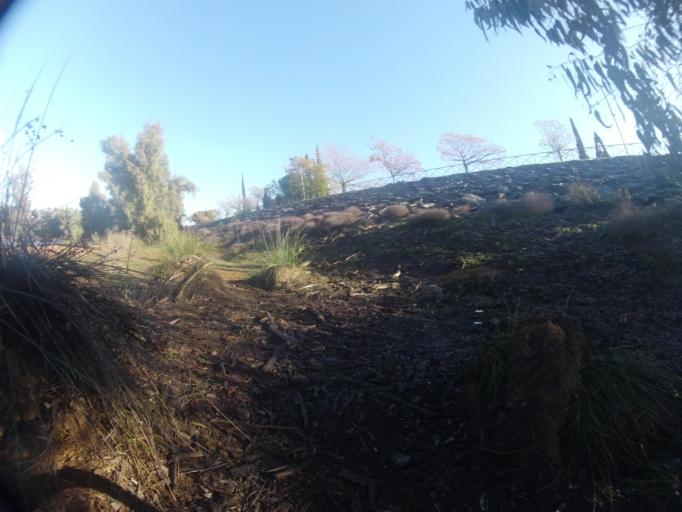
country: ES
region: Andalusia
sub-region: Provincia de Huelva
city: Gibraleon
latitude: 37.3716
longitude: -6.9757
